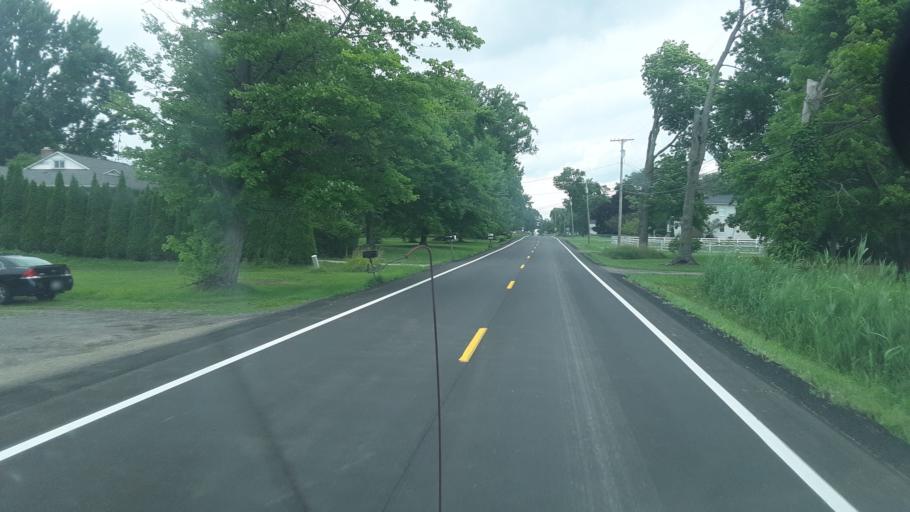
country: US
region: Ohio
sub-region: Trumbull County
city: Cortland
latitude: 41.3045
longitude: -80.6557
